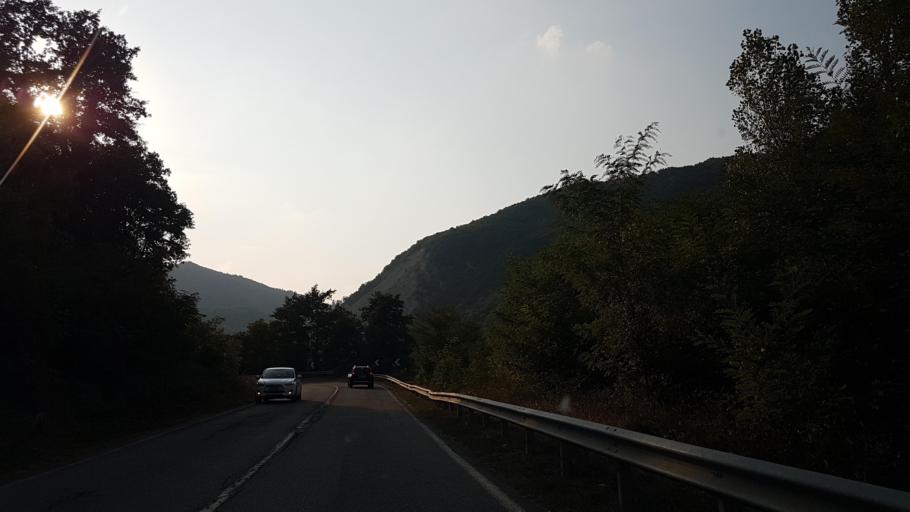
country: IT
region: Emilia-Romagna
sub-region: Provincia di Parma
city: Solignano
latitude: 44.6291
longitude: 10.0146
